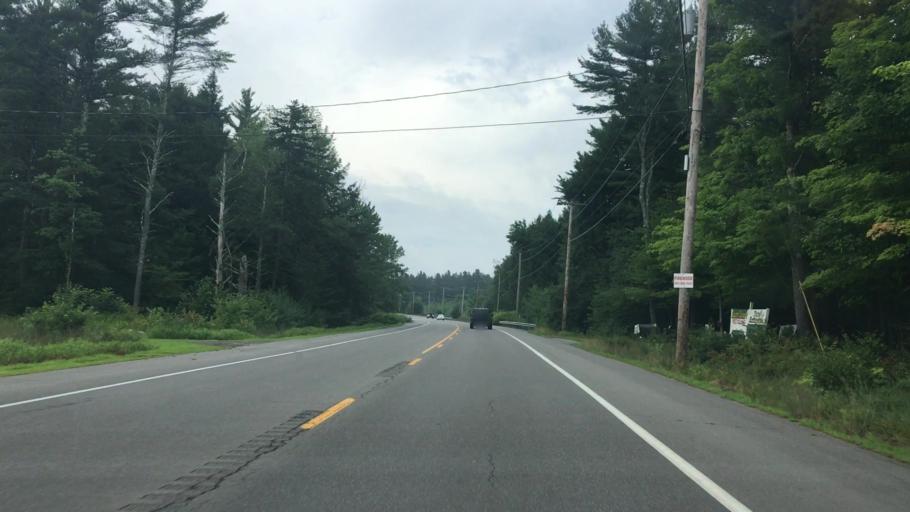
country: US
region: Maine
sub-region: York County
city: Lebanon
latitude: 43.4018
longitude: -70.8750
